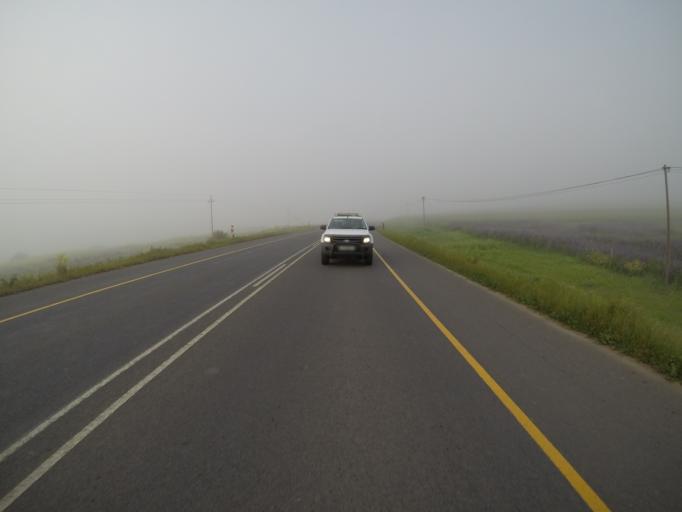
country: ZA
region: Western Cape
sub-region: City of Cape Town
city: Kraaifontein
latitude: -33.7680
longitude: 18.7127
